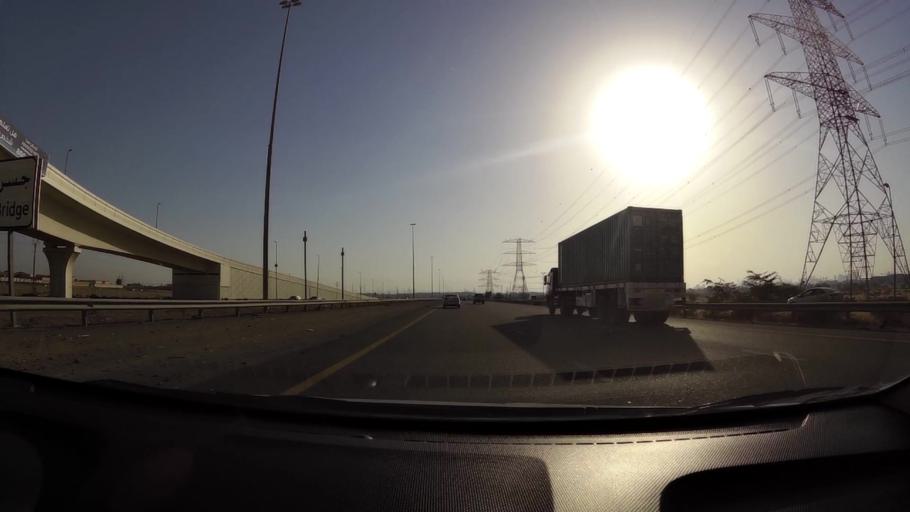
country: AE
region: Ajman
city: Ajman
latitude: 25.3590
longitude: 55.5132
